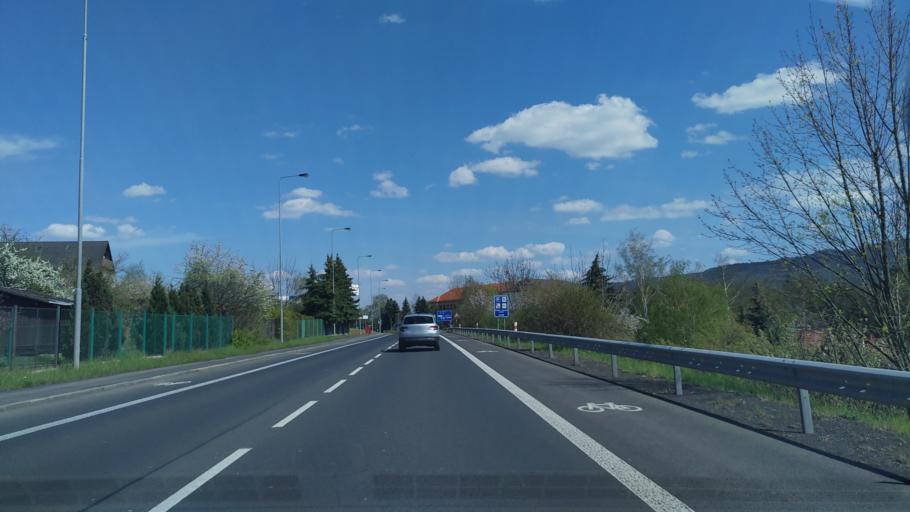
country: CZ
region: Ustecky
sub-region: Okres Chomutov
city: Klasterec nad Ohri
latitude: 50.3866
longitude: 13.1738
